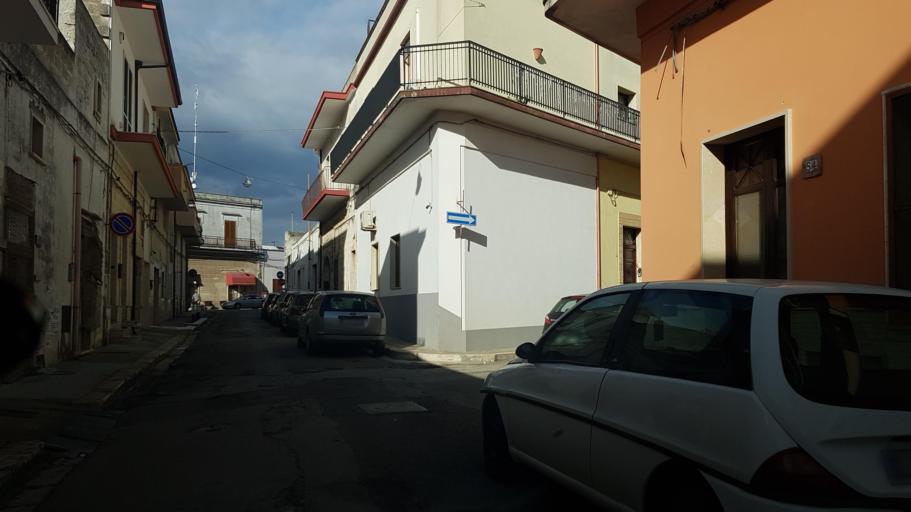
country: IT
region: Apulia
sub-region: Provincia di Brindisi
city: Torre Santa Susanna
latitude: 40.4685
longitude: 17.7400
